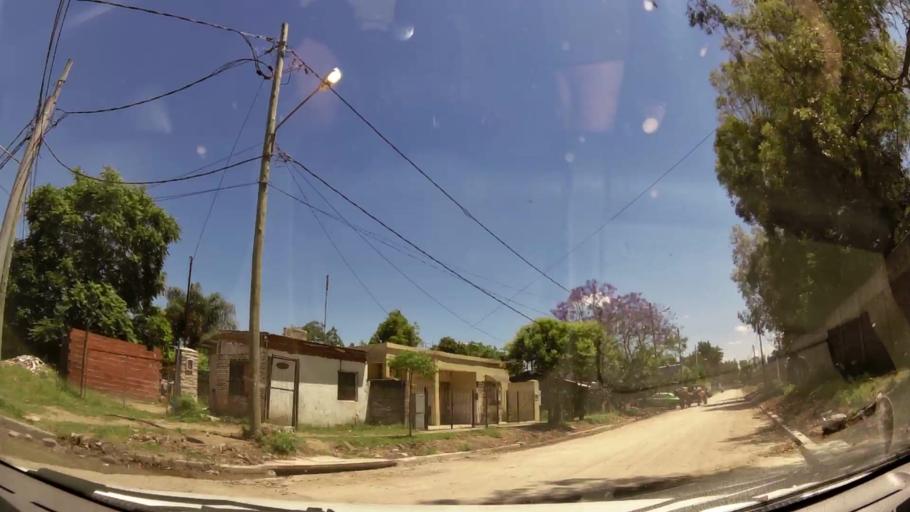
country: AR
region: Buenos Aires
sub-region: Partido de Merlo
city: Merlo
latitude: -34.6444
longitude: -58.7155
